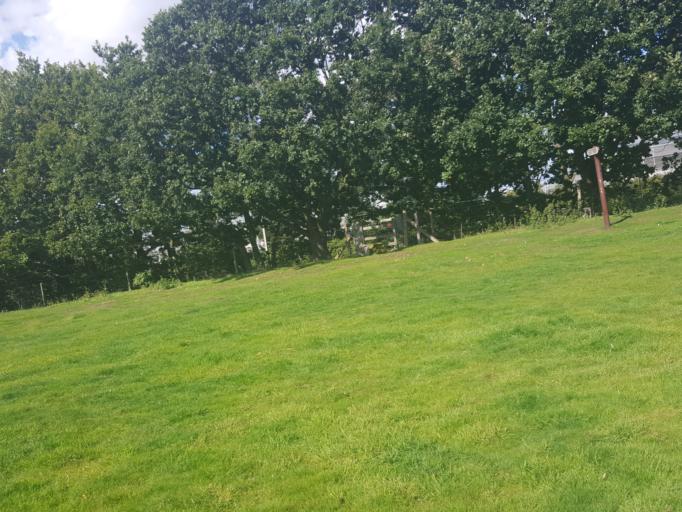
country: GB
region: England
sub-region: Essex
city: Alresford
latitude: 51.8522
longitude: 1.0195
